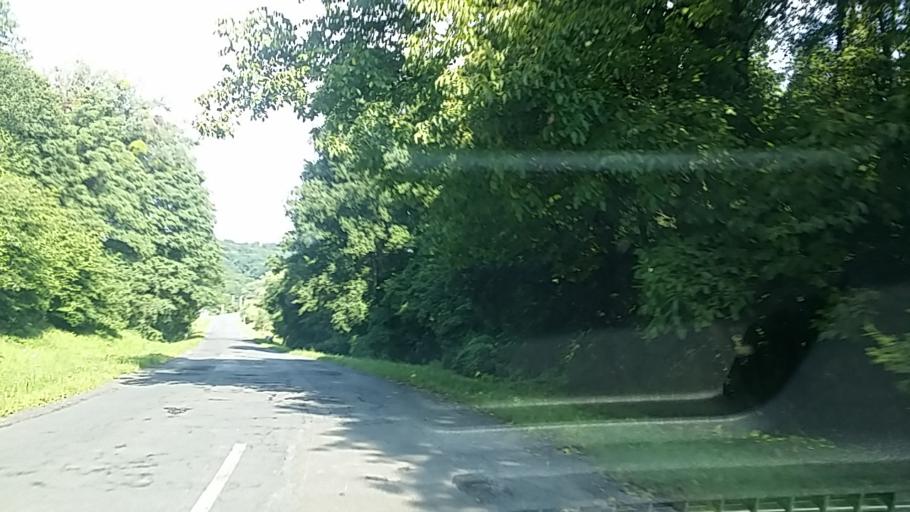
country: HU
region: Zala
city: Letenye
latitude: 46.5423
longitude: 16.7036
